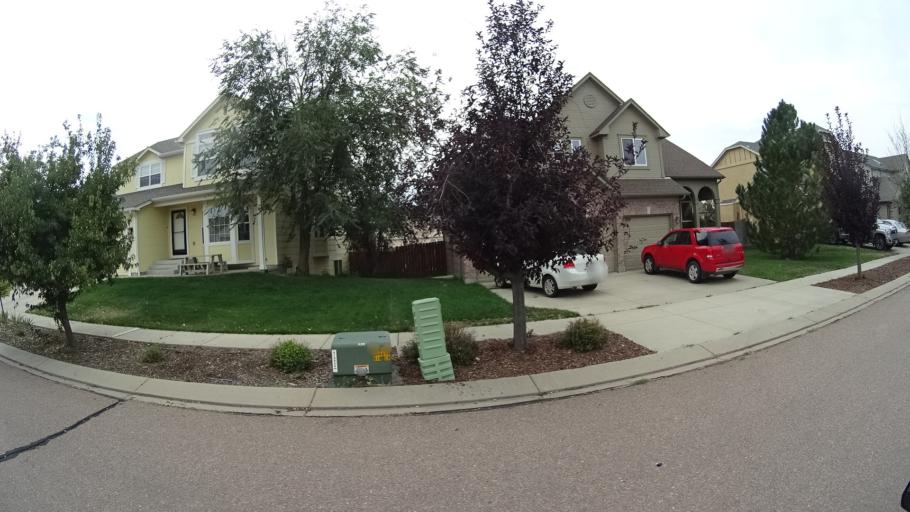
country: US
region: Colorado
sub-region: El Paso County
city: Cimarron Hills
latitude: 38.9145
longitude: -104.6911
